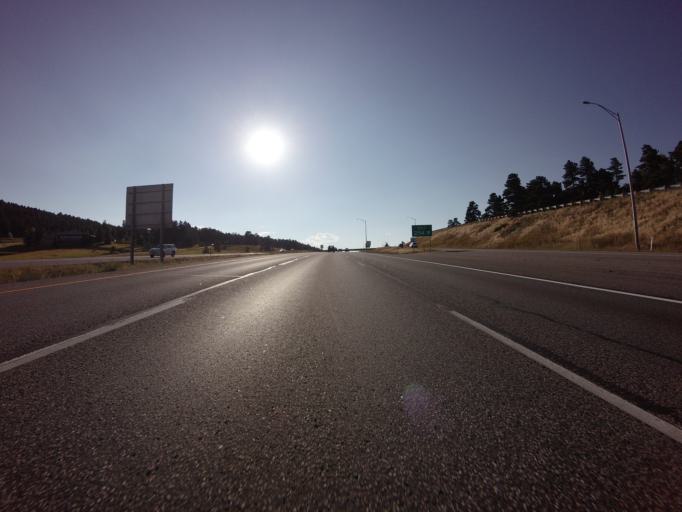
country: US
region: Colorado
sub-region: Jefferson County
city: Genesee
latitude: 39.7096
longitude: -105.2912
